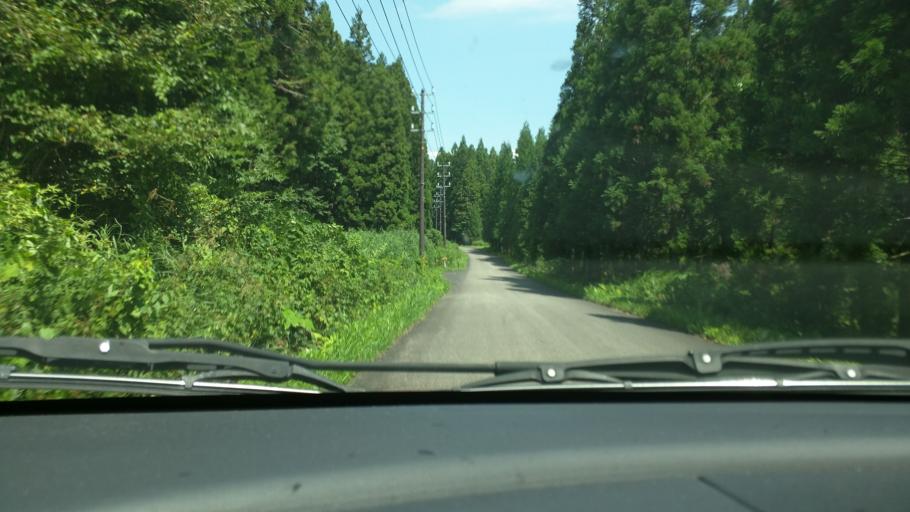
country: JP
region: Fukushima
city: Inawashiro
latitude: 37.3617
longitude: 140.0576
